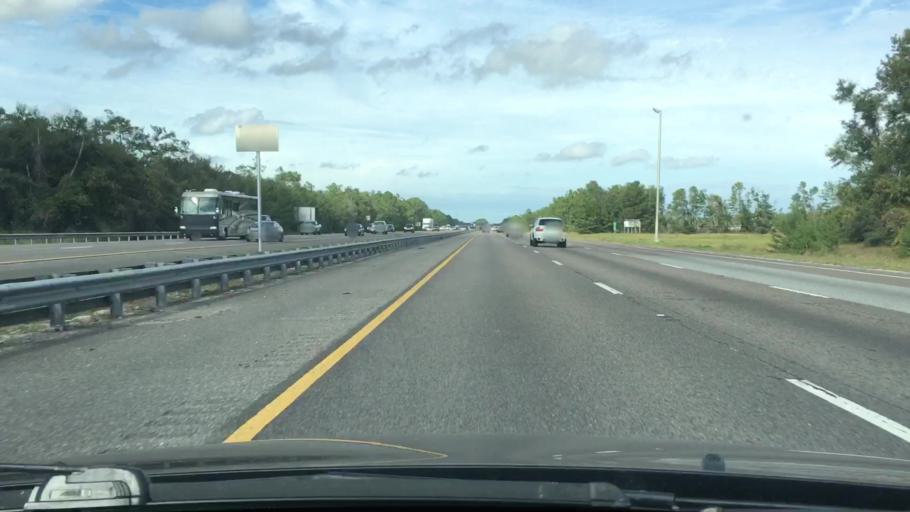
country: US
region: Florida
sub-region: Volusia County
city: Ormond Beach
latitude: 29.2644
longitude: -81.1185
